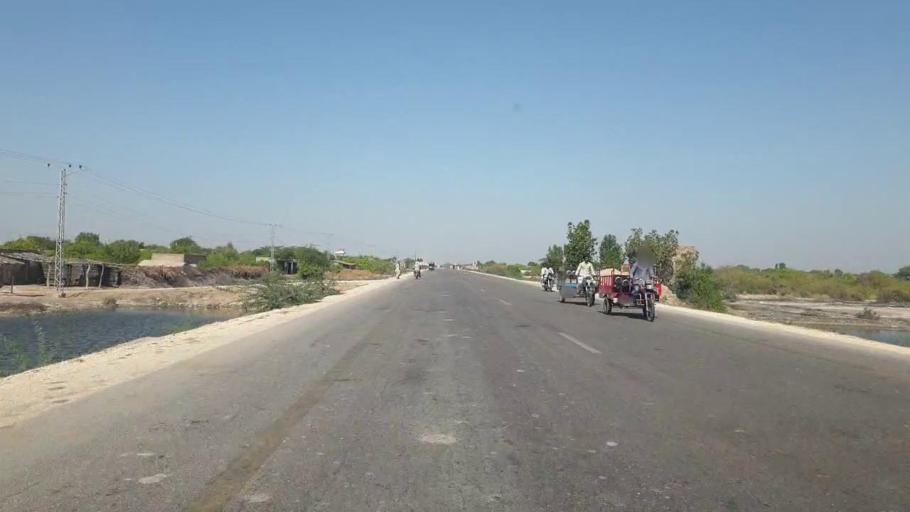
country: PK
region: Sindh
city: Talhar
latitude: 24.8497
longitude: 68.8164
